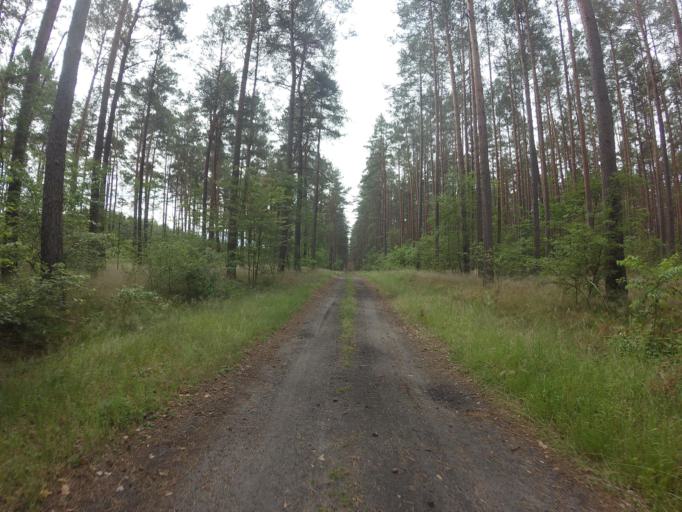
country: PL
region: West Pomeranian Voivodeship
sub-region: Powiat choszczenski
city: Bierzwnik
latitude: 53.1189
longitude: 15.6882
